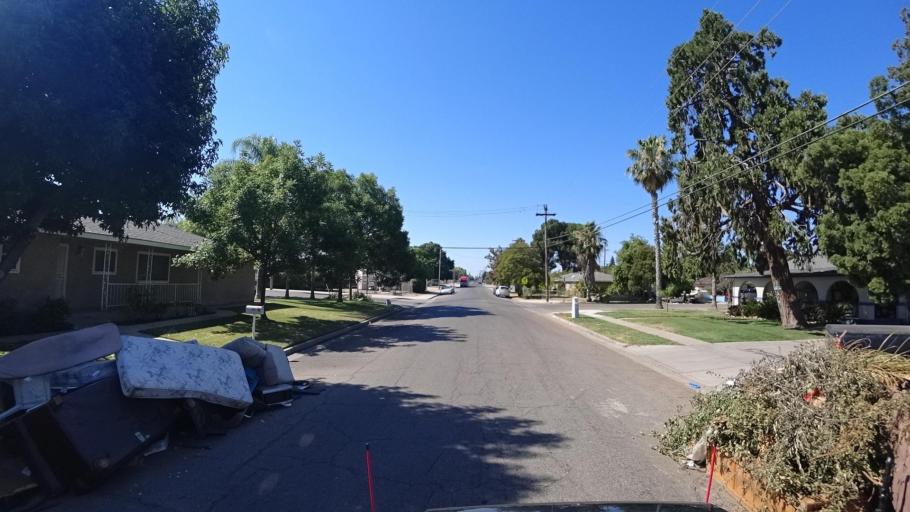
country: US
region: California
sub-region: Fresno County
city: Tarpey Village
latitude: 36.7835
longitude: -119.7408
